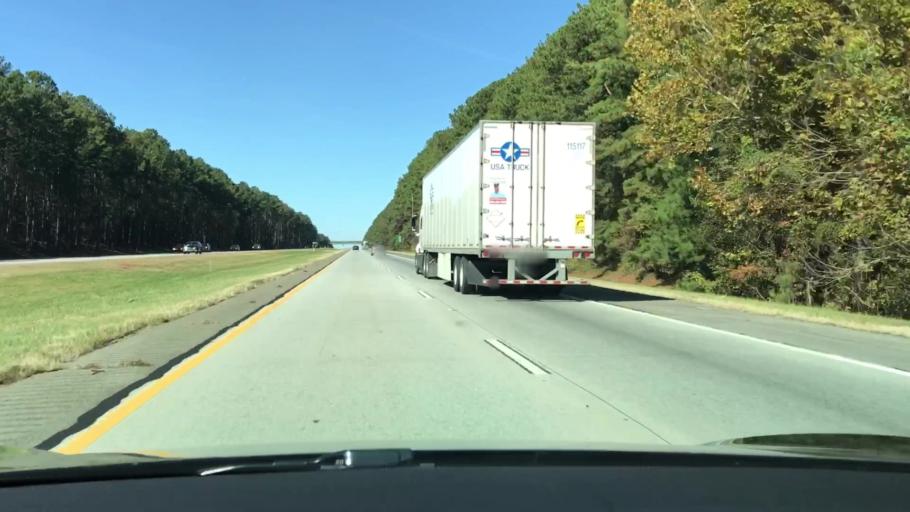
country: US
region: Georgia
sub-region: Taliaferro County
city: Crawfordville
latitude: 33.5085
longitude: -82.8392
